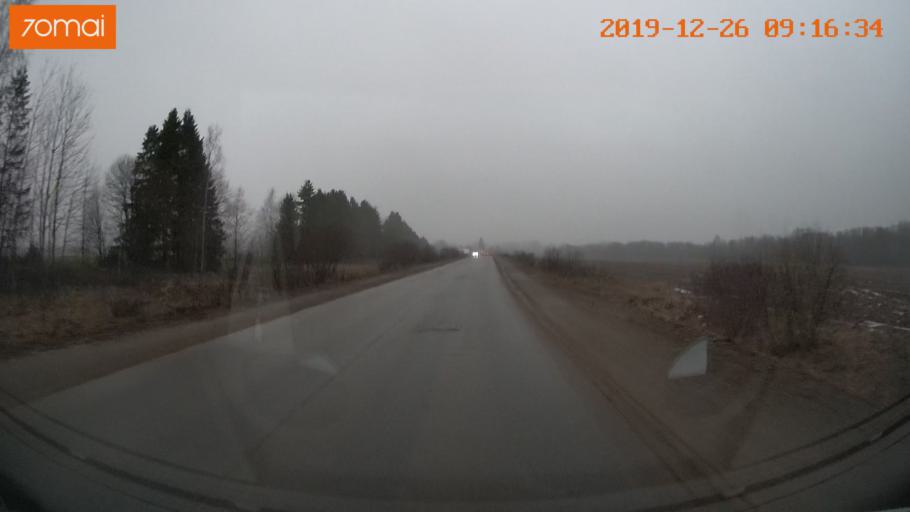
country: RU
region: Vologda
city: Gryazovets
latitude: 58.9201
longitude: 40.2390
